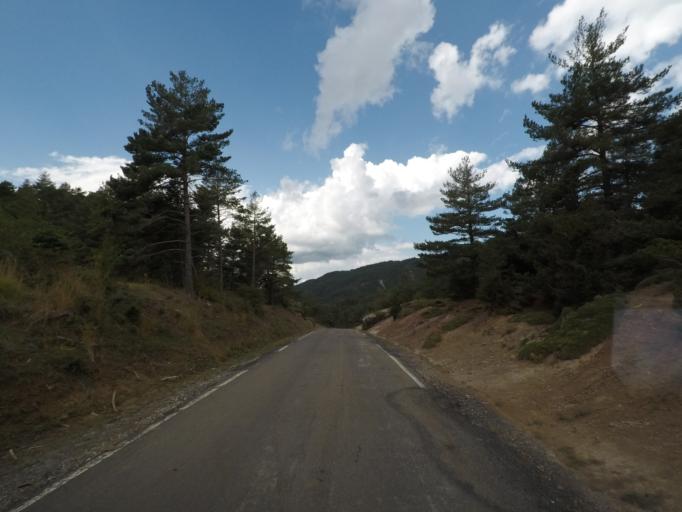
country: ES
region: Aragon
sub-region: Provincia de Huesca
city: Fiscal
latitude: 42.4040
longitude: -0.0662
